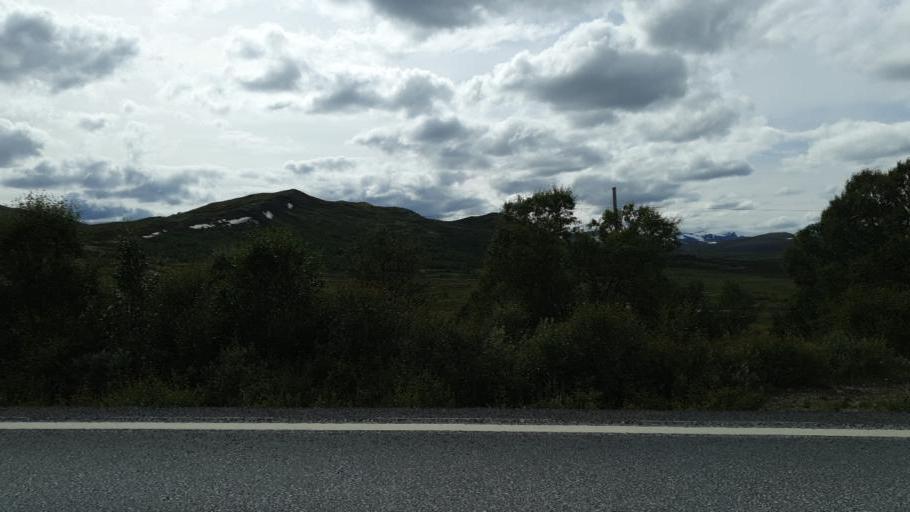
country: NO
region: Oppland
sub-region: Dovre
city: Dovre
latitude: 62.2349
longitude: 9.5298
